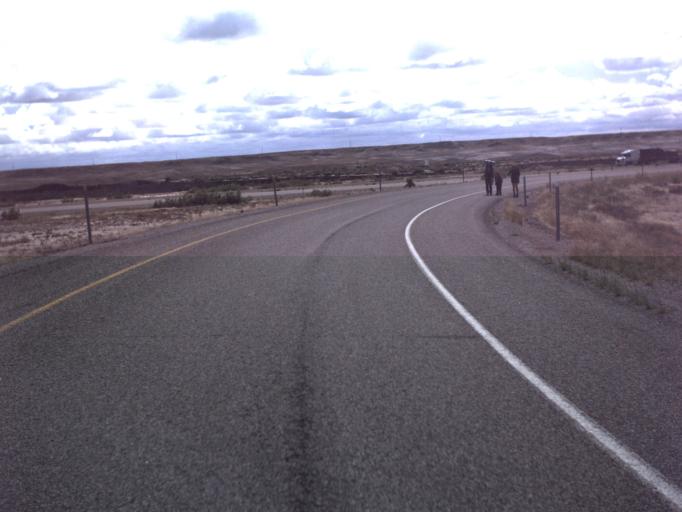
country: US
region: Utah
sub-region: Carbon County
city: East Carbon City
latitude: 38.9821
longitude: -110.2366
